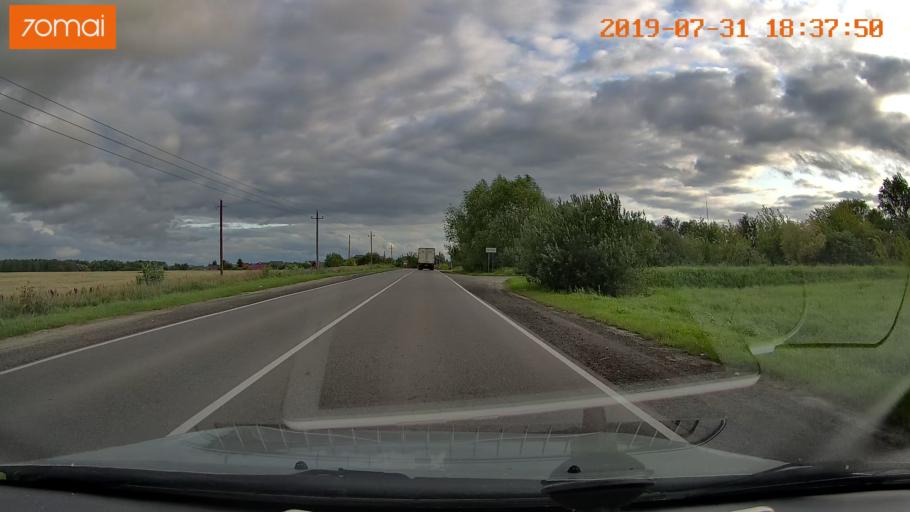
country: RU
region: Moskovskaya
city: Voskresensk
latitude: 55.2759
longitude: 38.6588
